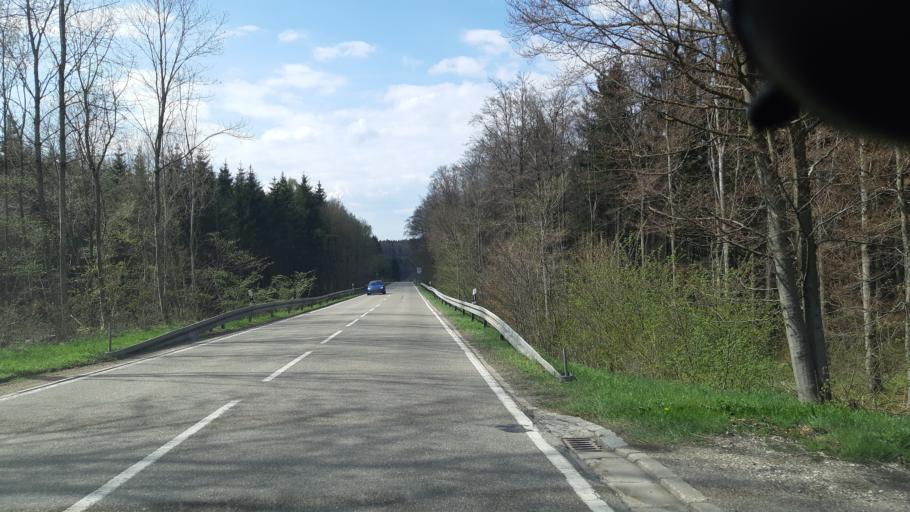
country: DE
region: Baden-Wuerttemberg
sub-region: Regierungsbezirk Stuttgart
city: Oberkochen
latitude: 48.8000
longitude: 10.1554
